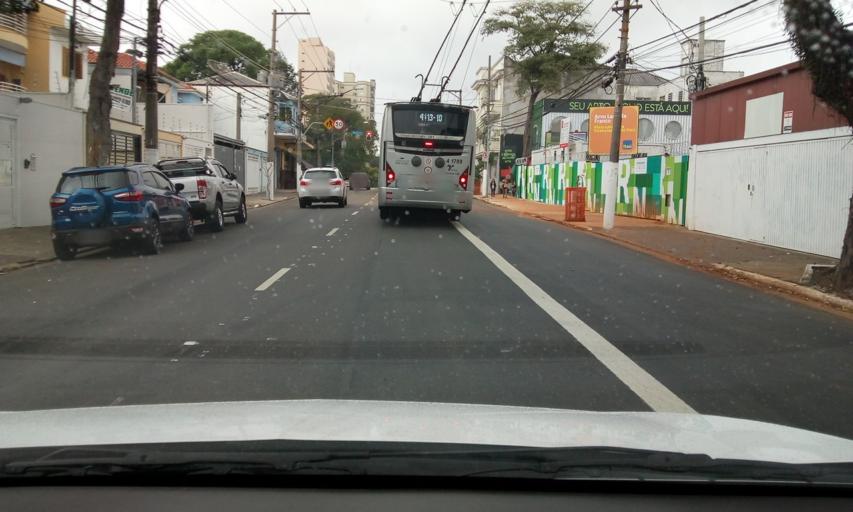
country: BR
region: Sao Paulo
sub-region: Sao Paulo
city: Sao Paulo
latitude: -23.5761
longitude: -46.6251
